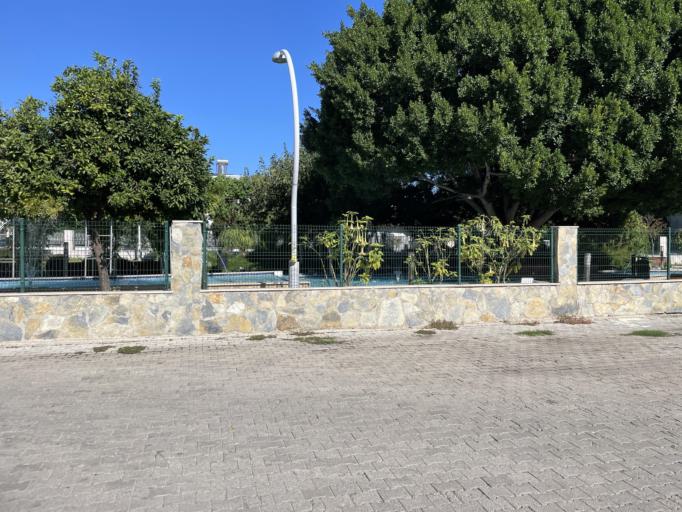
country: TR
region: Antalya
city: Kemer
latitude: 36.5981
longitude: 30.5643
